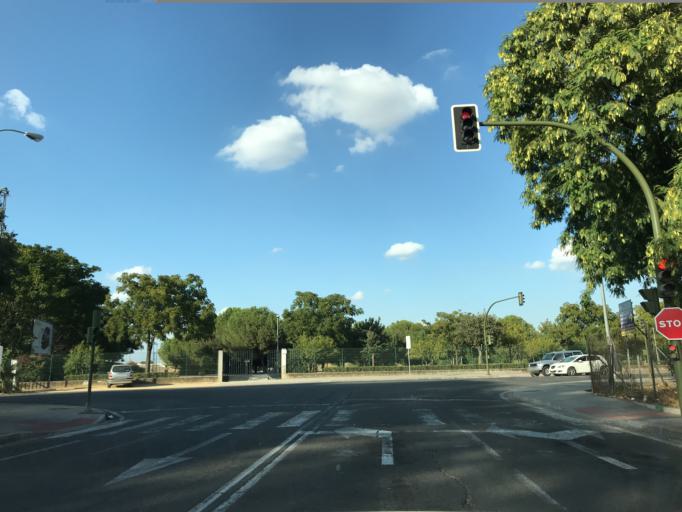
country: ES
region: Andalusia
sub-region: Provincia de Sevilla
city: Sevilla
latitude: 37.4129
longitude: -5.9251
